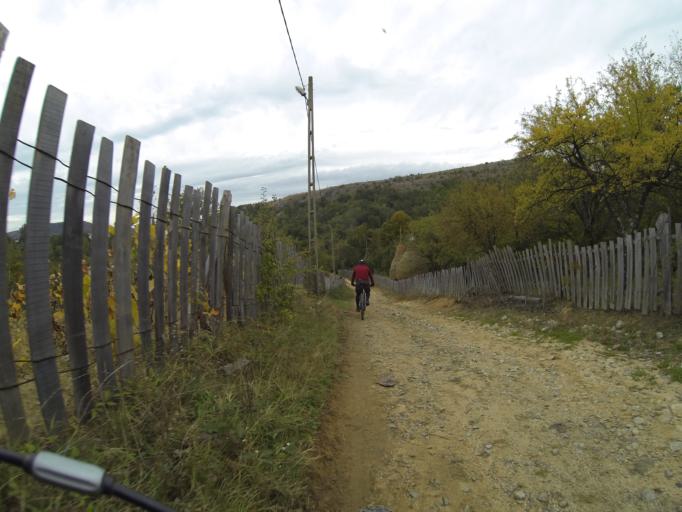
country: RO
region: Gorj
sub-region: Comuna Tismana
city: Sohodol
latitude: 45.0586
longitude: 22.8880
